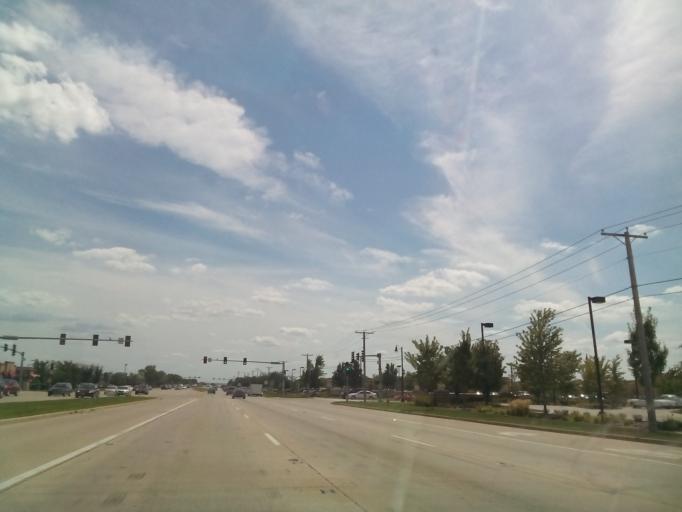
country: US
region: Illinois
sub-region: Will County
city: Plainfield
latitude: 41.7140
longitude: -88.2060
